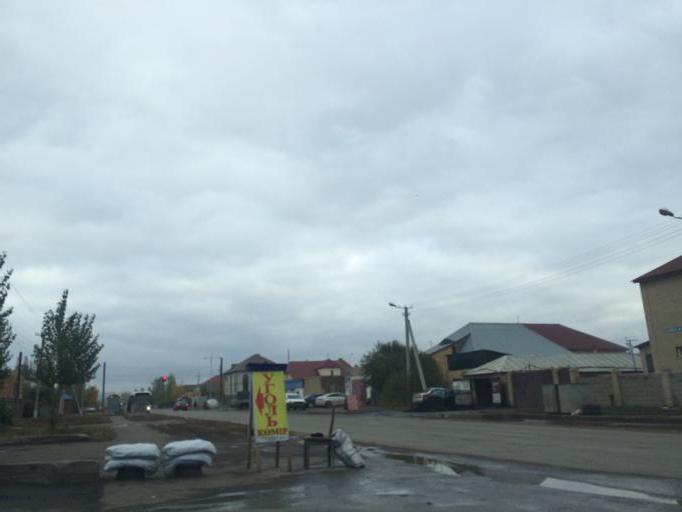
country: KZ
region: Astana Qalasy
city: Astana
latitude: 51.1360
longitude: 71.5003
